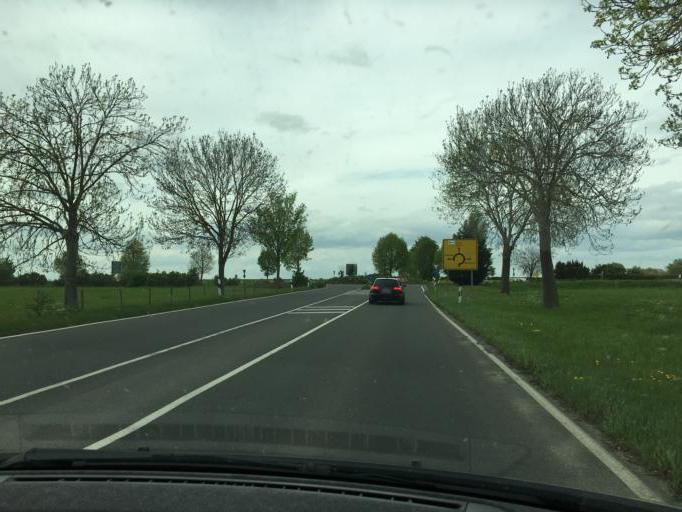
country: DE
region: North Rhine-Westphalia
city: Zulpich
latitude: 50.7031
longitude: 6.7145
